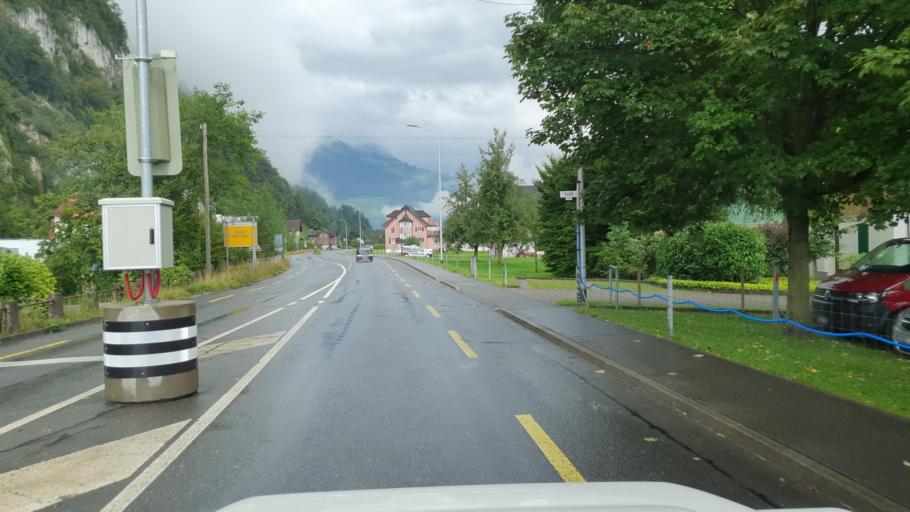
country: CH
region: Nidwalden
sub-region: Nidwalden
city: Stansstad
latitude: 46.9745
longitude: 8.3439
